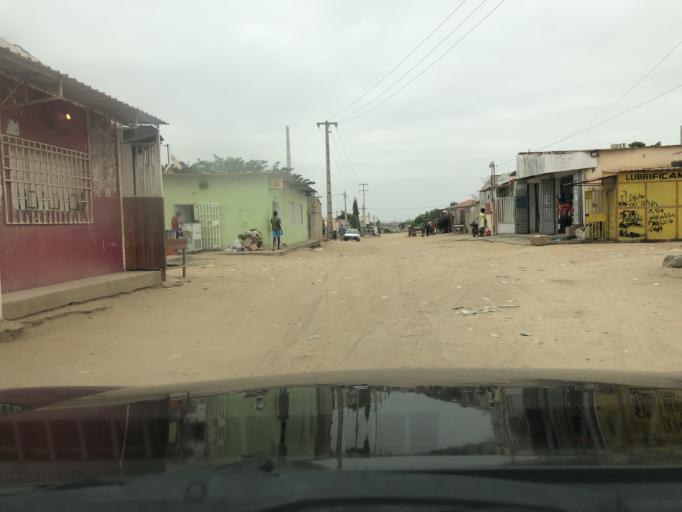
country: AO
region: Luanda
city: Luanda
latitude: -8.9377
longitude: 13.2308
